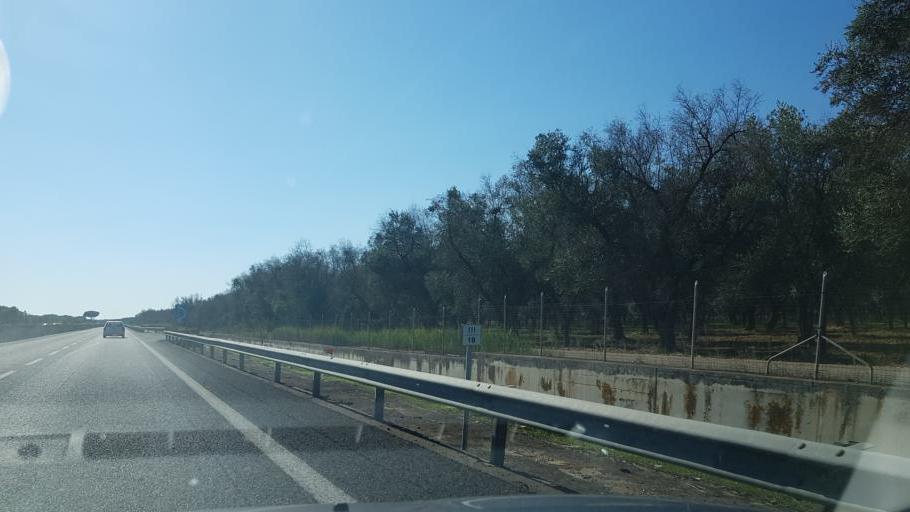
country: IT
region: Apulia
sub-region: Provincia di Brindisi
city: Torchiarolo
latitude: 40.4765
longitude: 18.0471
